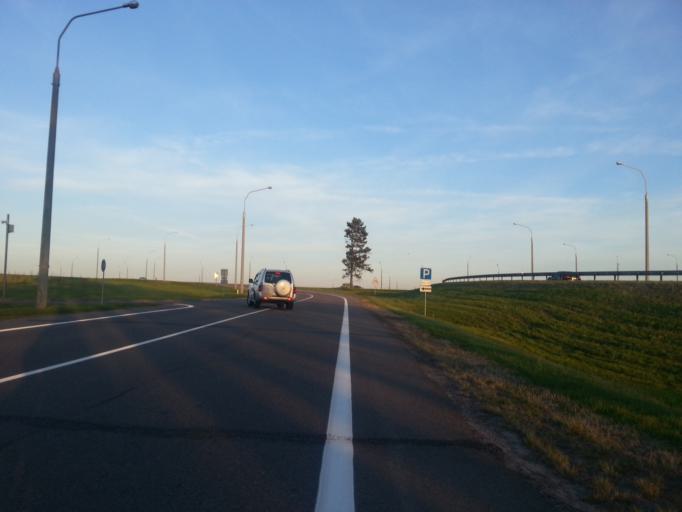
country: BY
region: Minsk
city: Slabada
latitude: 54.0180
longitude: 27.8923
